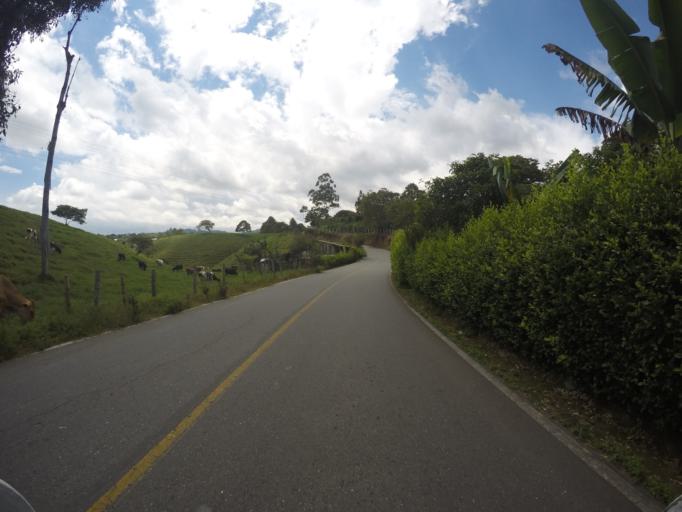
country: CO
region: Quindio
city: Filandia
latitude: 4.6356
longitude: -75.7026
